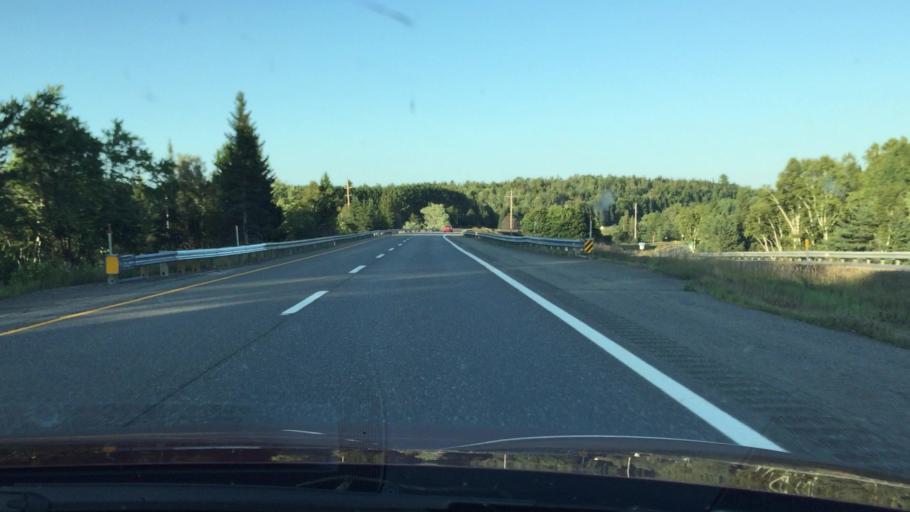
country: US
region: Maine
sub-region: Aroostook County
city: Hodgdon
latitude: 46.1436
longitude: -68.0623
